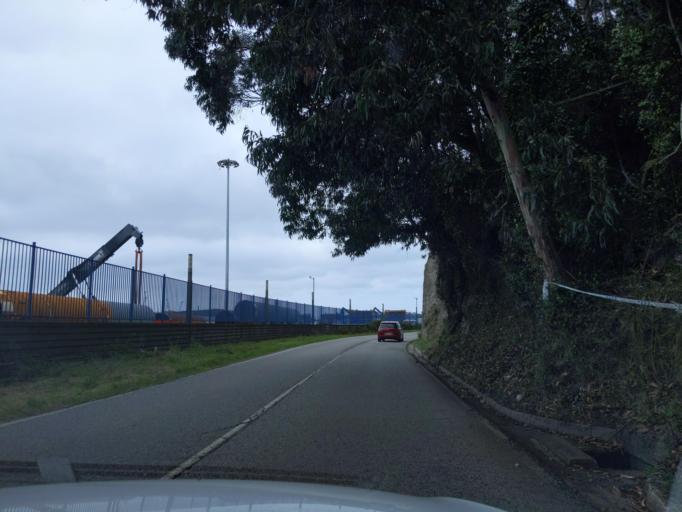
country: ES
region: Asturias
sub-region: Province of Asturias
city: Aviles
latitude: 43.5773
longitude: -5.9188
